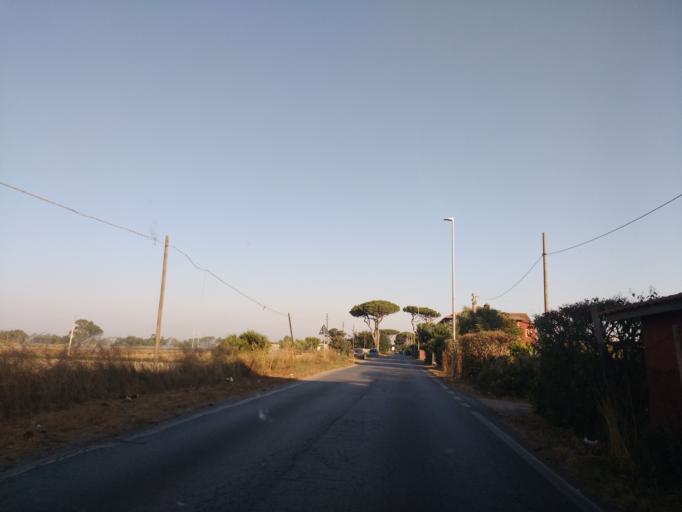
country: IT
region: Latium
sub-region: Citta metropolitana di Roma Capitale
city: Maccarese
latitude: 41.8614
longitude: 12.2118
